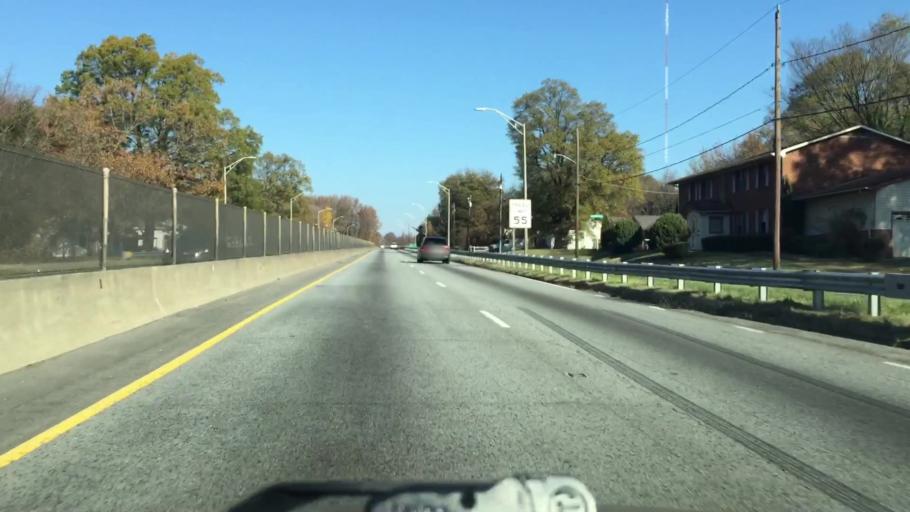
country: US
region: North Carolina
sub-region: Guilford County
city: Greensboro
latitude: 36.0937
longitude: -79.7656
